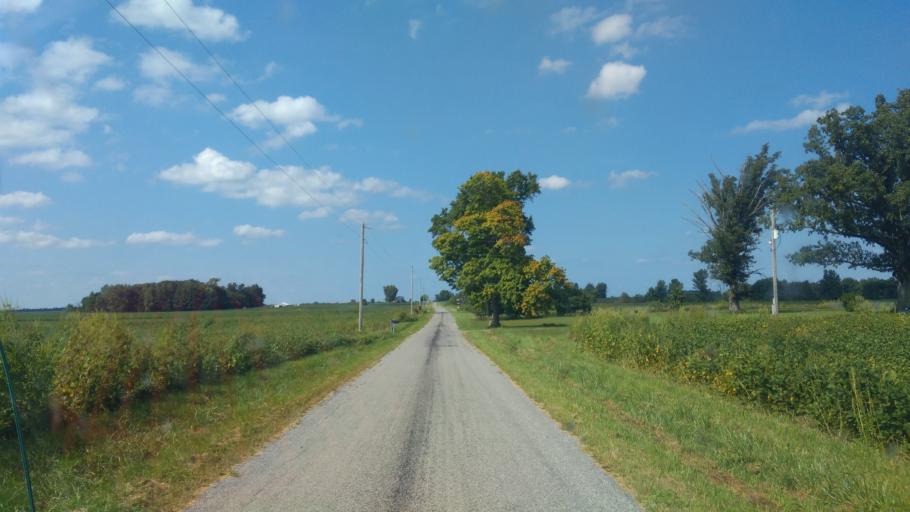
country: US
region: Ohio
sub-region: Union County
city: Richwood
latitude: 40.5030
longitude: -83.4499
